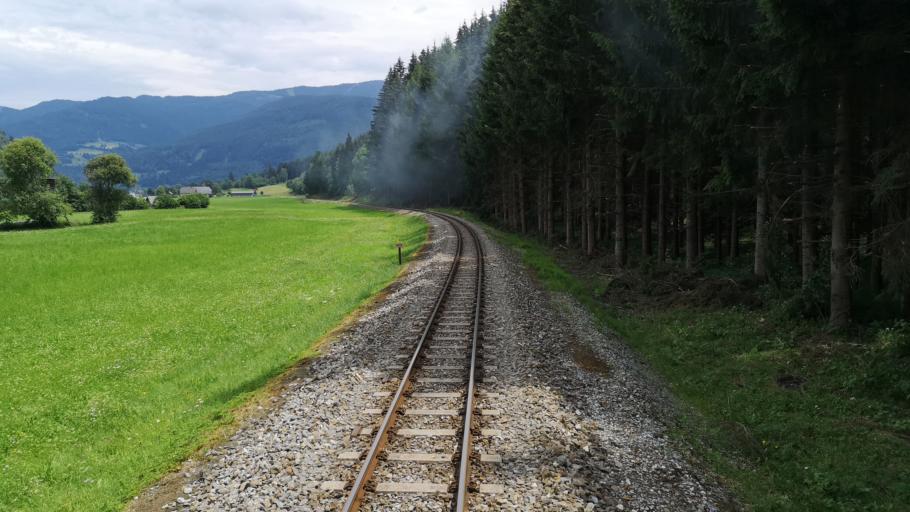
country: AT
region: Styria
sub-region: Politischer Bezirk Murau
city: Stadl an der Mur
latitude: 47.0840
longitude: 13.9474
